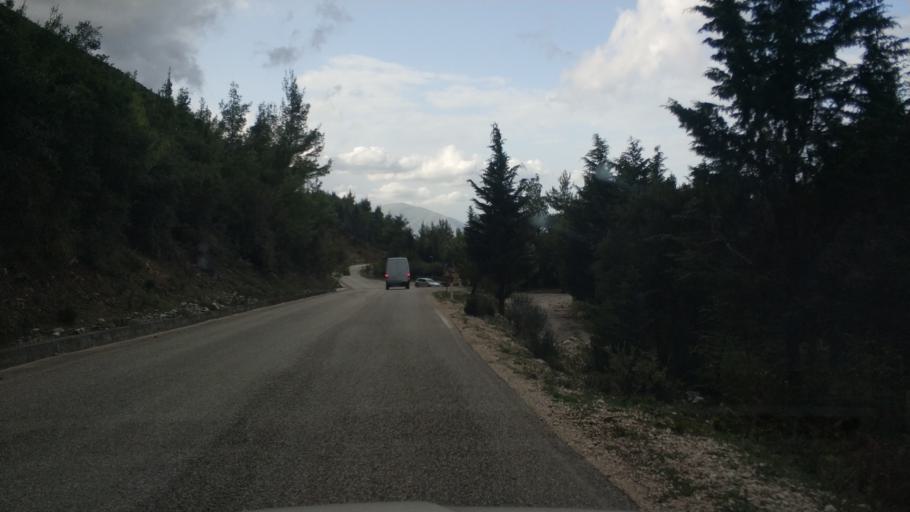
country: AL
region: Vlore
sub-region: Rrethi i Vlores
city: Orikum
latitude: 40.2560
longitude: 19.5302
